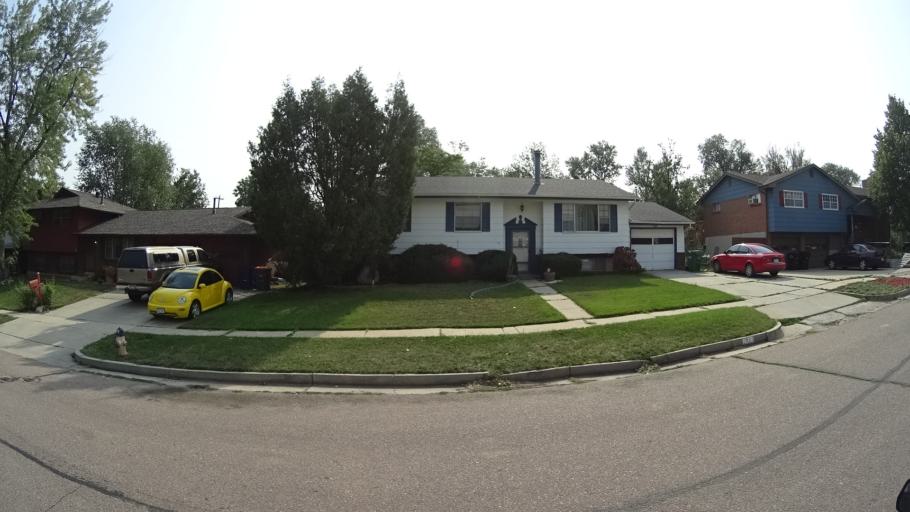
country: US
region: Colorado
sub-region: El Paso County
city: Stratmoor
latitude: 38.8163
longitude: -104.7743
